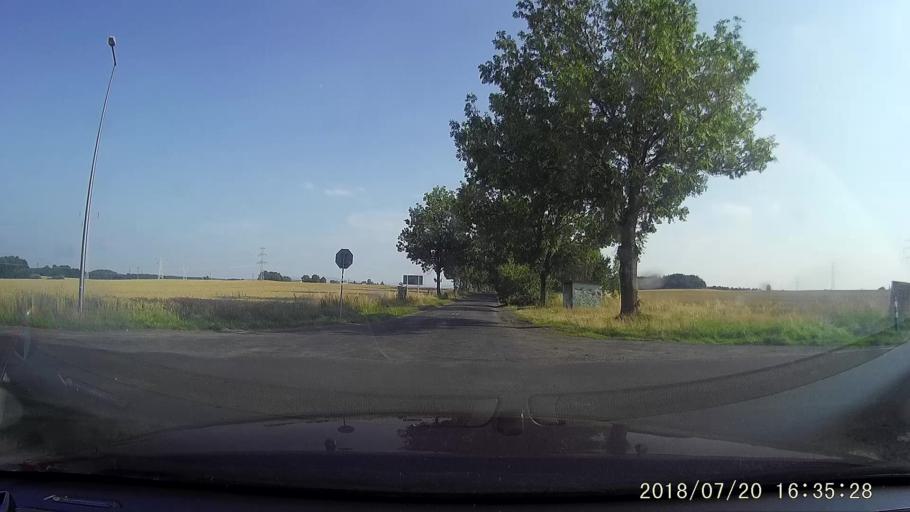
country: PL
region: Lower Silesian Voivodeship
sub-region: Powiat zgorzelecki
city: Sulikow
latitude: 51.0792
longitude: 15.1028
